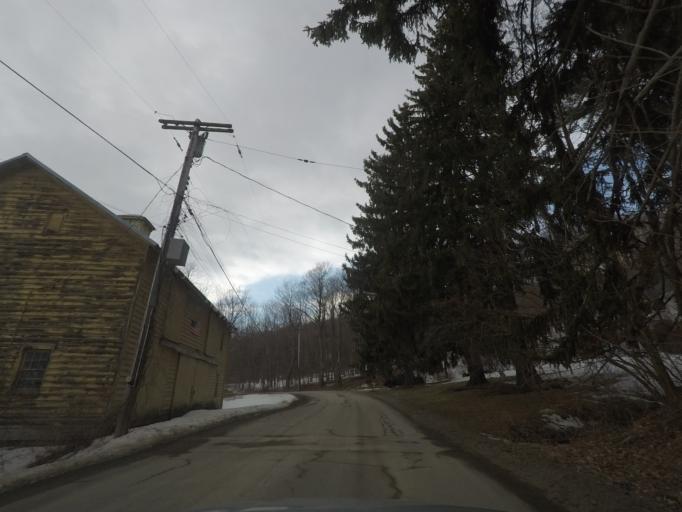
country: US
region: New York
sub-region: Saratoga County
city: Waterford
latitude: 42.7829
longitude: -73.6196
